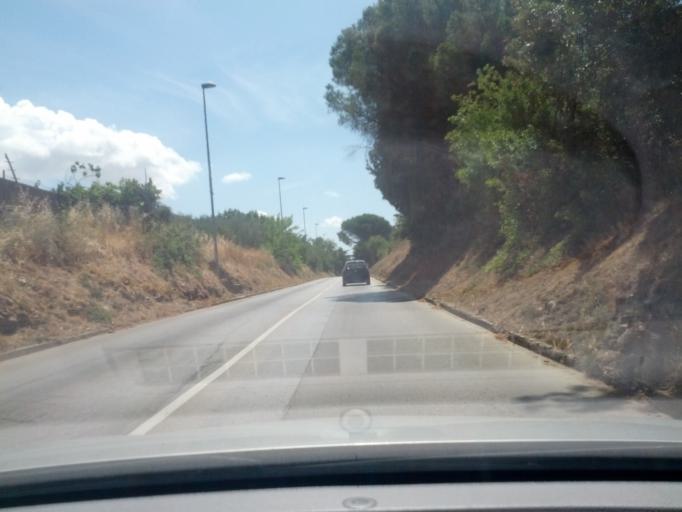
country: HR
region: Istarska
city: Fazana
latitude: 44.9129
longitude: 13.8190
